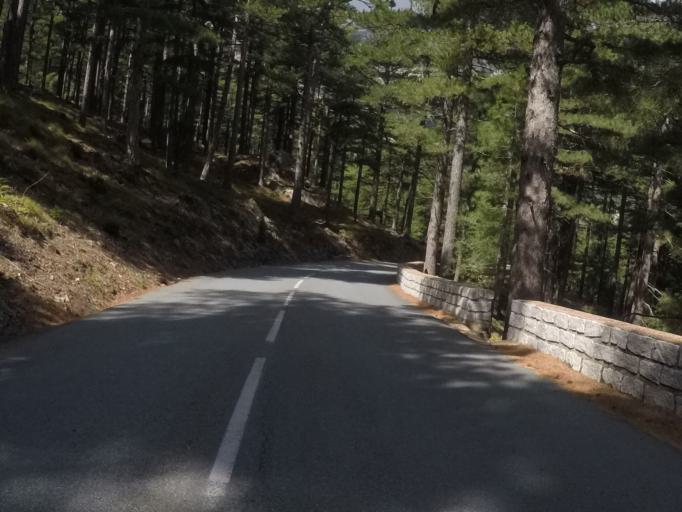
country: FR
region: Corsica
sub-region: Departement de la Corse-du-Sud
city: Zonza
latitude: 41.7963
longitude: 9.2323
